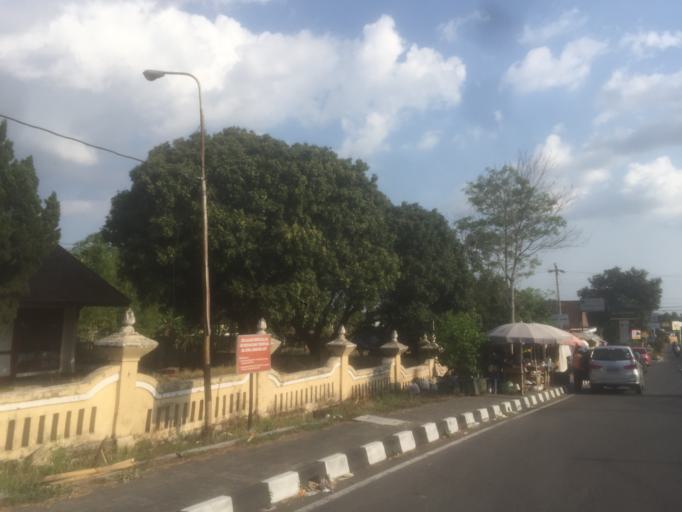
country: ID
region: Daerah Istimewa Yogyakarta
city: Sleman
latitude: -7.6634
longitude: 110.4203
